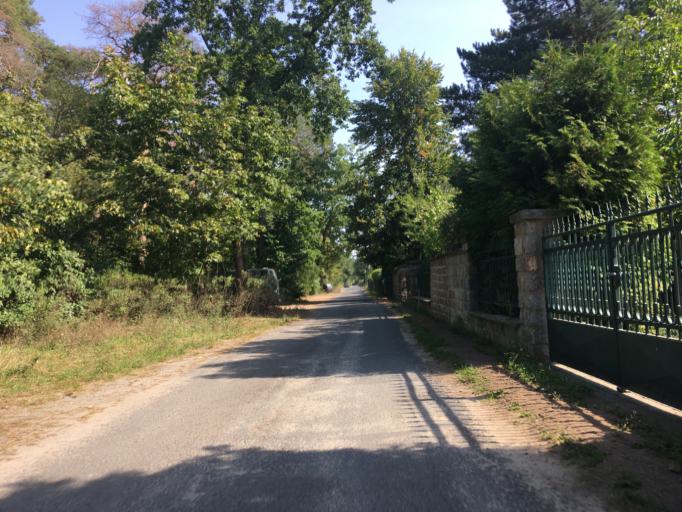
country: DE
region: Berlin
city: Schmockwitz
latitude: 52.3768
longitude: 13.6373
